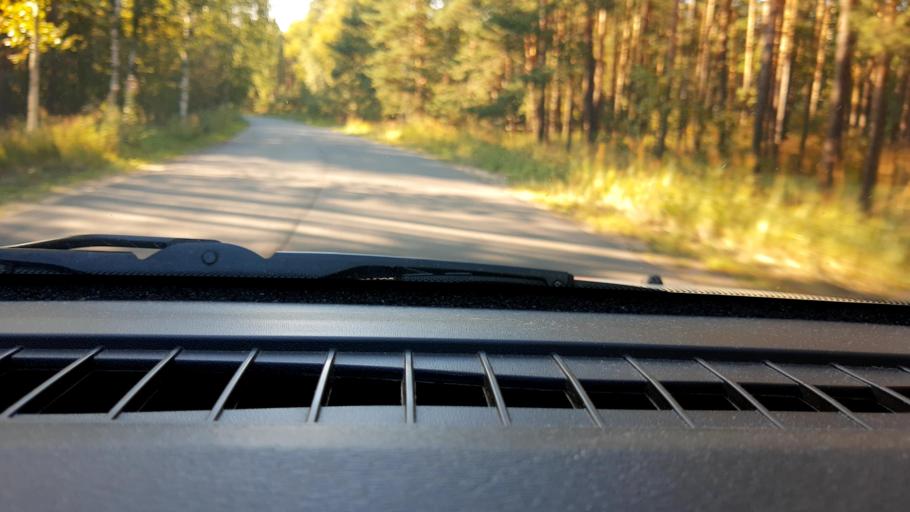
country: RU
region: Nizjnij Novgorod
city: Babino
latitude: 56.3282
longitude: 43.6326
